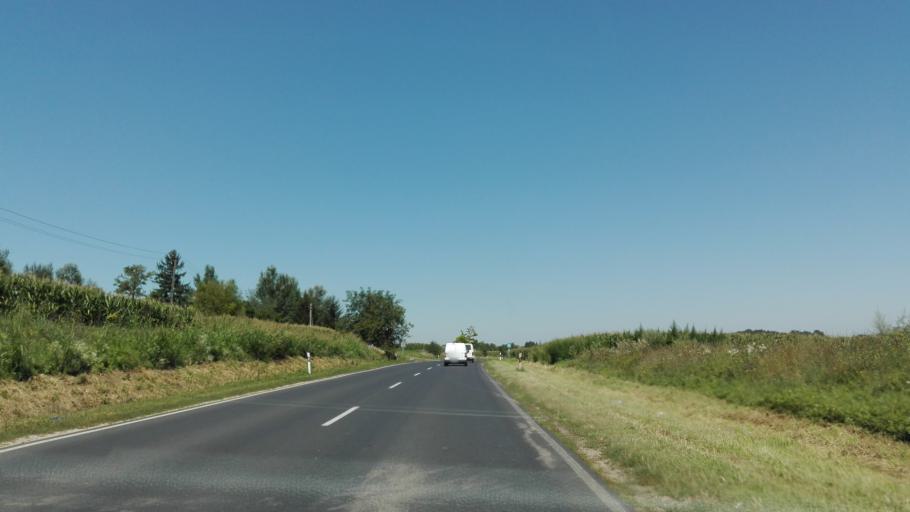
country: HU
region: Fejer
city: Mezoszilas
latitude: 46.7960
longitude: 18.4926
